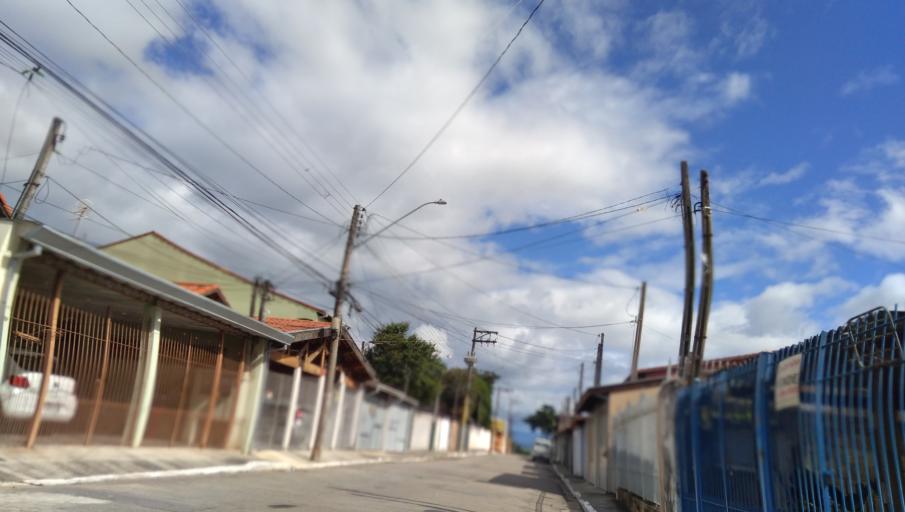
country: BR
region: Sao Paulo
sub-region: Sao Jose Dos Campos
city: Sao Jose dos Campos
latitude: -23.1757
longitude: -45.8534
